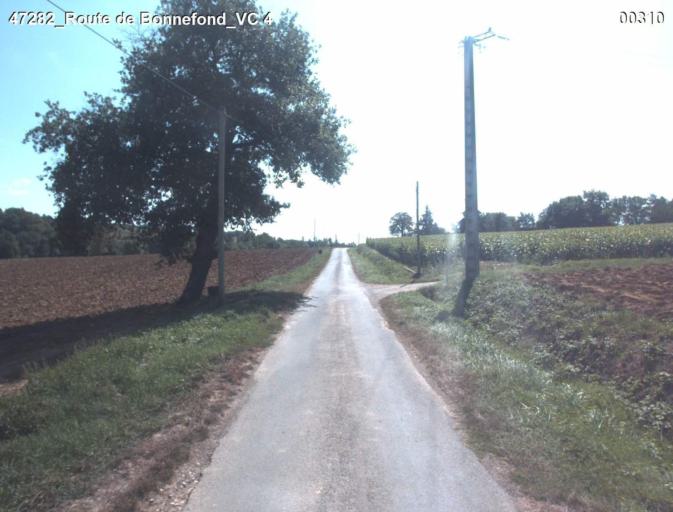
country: FR
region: Aquitaine
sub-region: Departement du Lot-et-Garonne
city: Laplume
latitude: 44.1074
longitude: 0.4754
